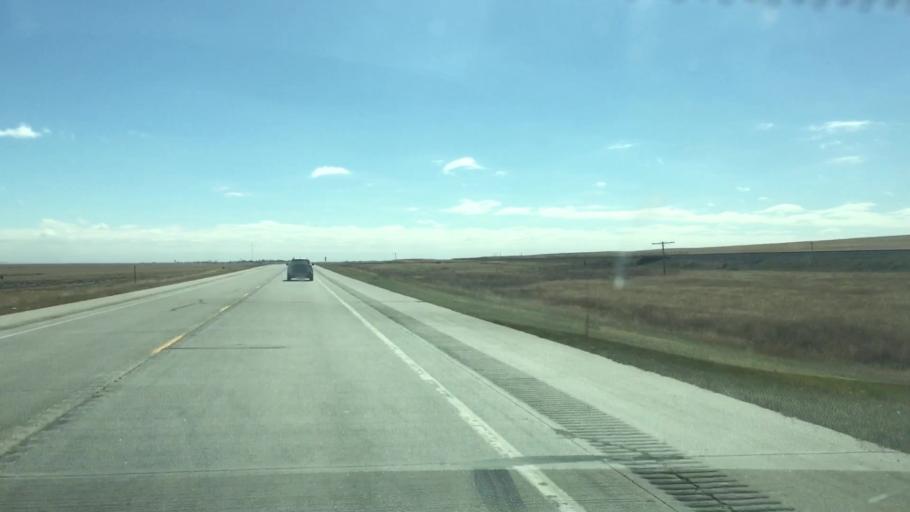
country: US
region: Colorado
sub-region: Lincoln County
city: Hugo
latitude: 39.1717
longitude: -103.5333
